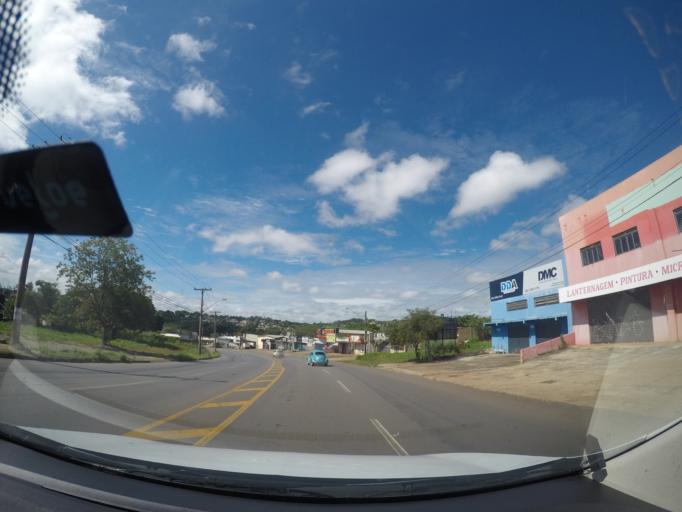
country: BR
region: Goias
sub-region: Goiania
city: Goiania
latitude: -16.6301
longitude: -49.2853
